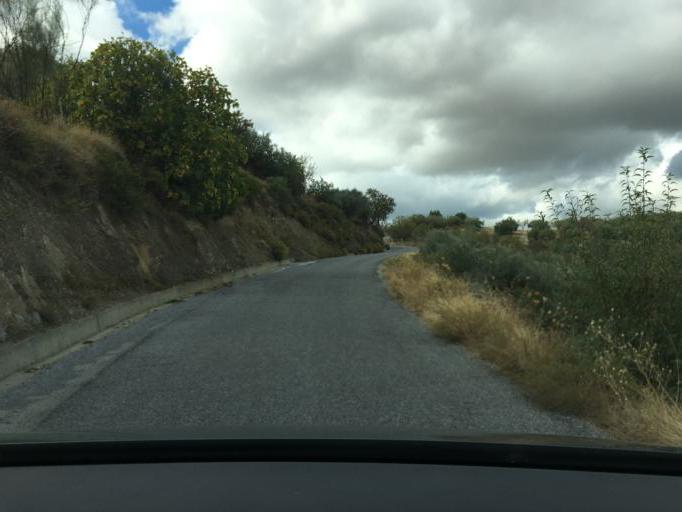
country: ES
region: Andalusia
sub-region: Provincia de Granada
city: Quentar
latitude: 37.2019
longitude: -3.4711
